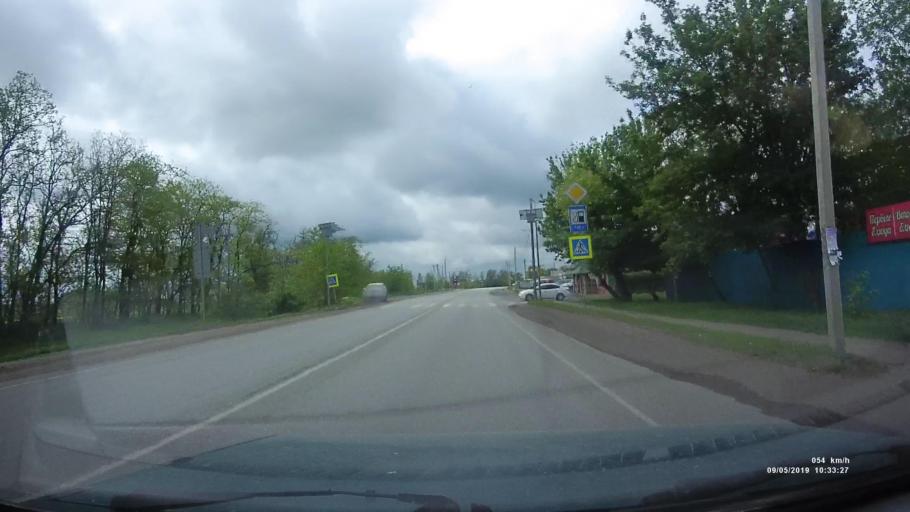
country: RU
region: Rostov
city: Azov
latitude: 47.0636
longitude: 39.4248
